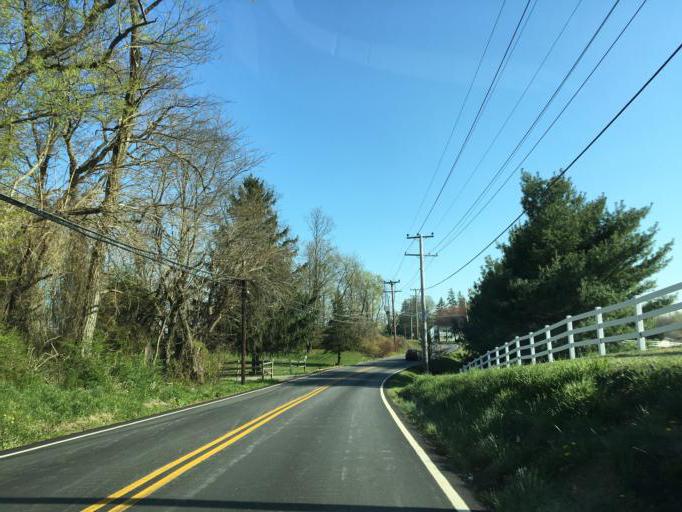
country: US
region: Maryland
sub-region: Baltimore County
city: Hampton
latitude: 39.4977
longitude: -76.5267
